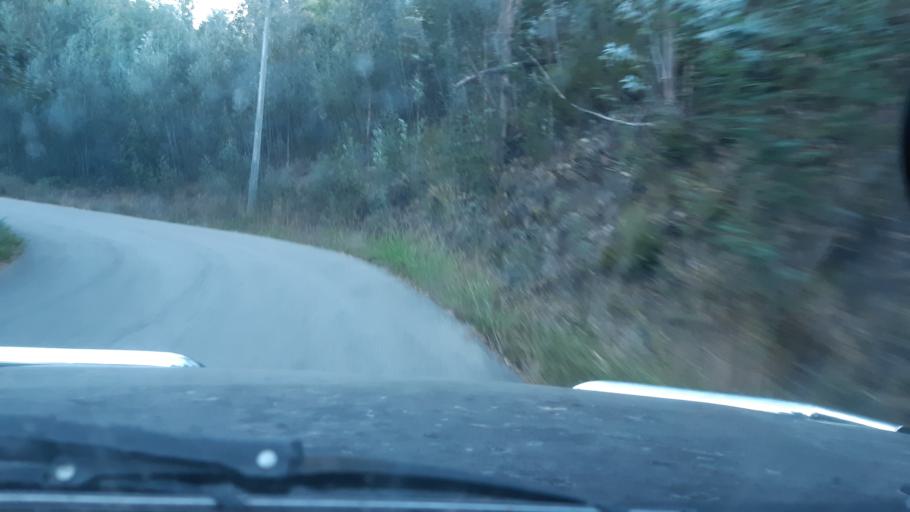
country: PT
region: Aveiro
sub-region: Agueda
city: Aguada de Cima
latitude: 40.5674
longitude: -8.3630
